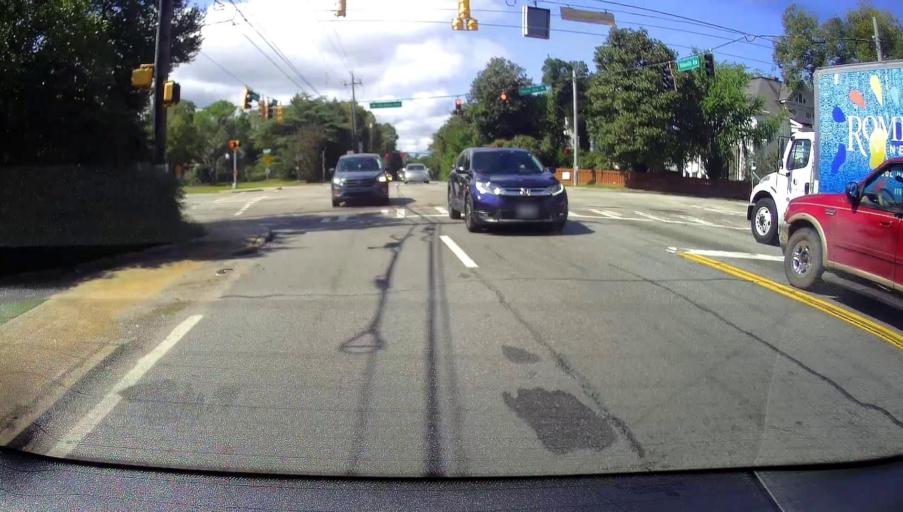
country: US
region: Georgia
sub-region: Bibb County
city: Macon
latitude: 32.8461
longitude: -83.6623
